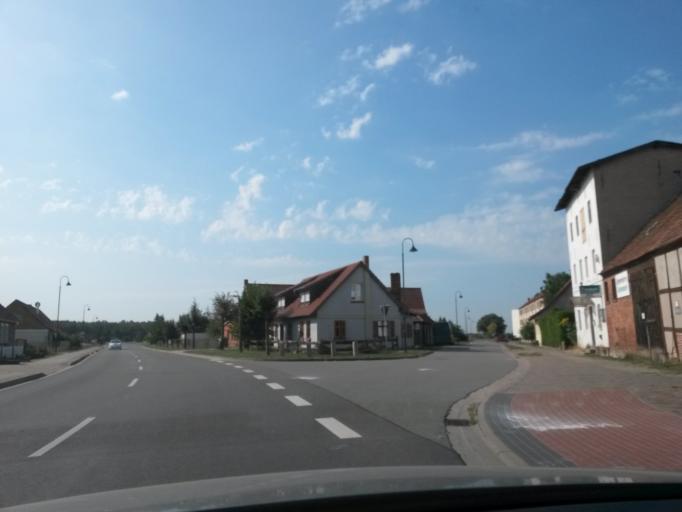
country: DE
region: Saxony-Anhalt
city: Jerichow
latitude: 52.5372
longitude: 12.0153
